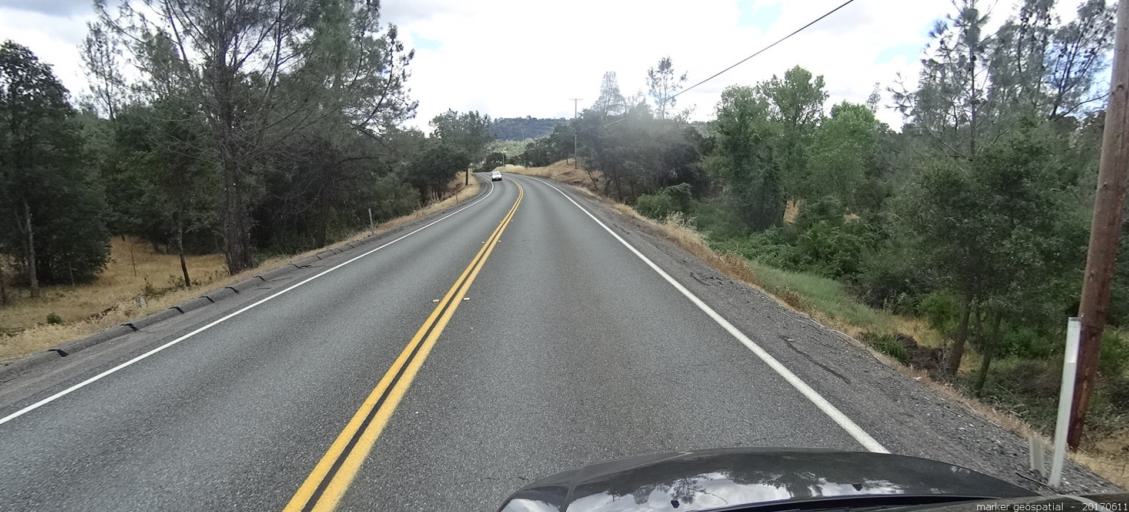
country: US
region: California
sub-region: Butte County
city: Paradise
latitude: 39.6544
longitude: -121.5641
